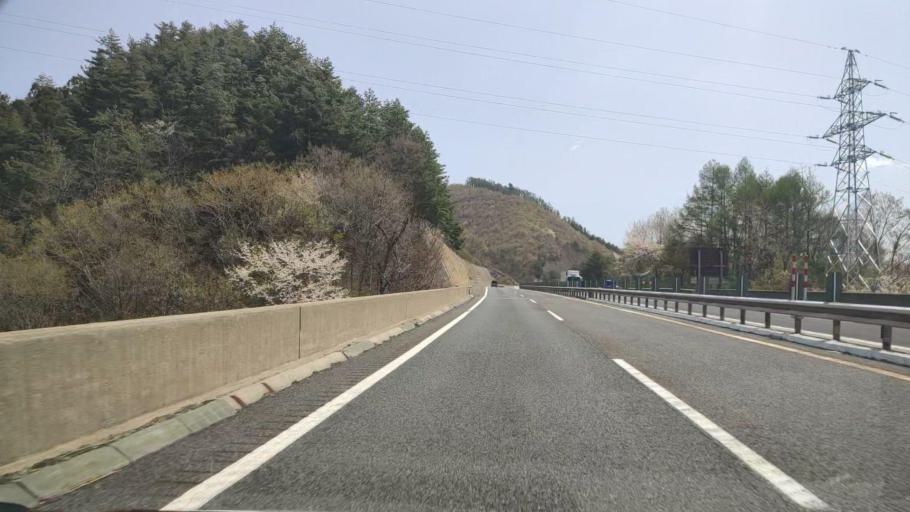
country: JP
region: Iwate
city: Ichinohe
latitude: 40.2314
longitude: 141.3075
